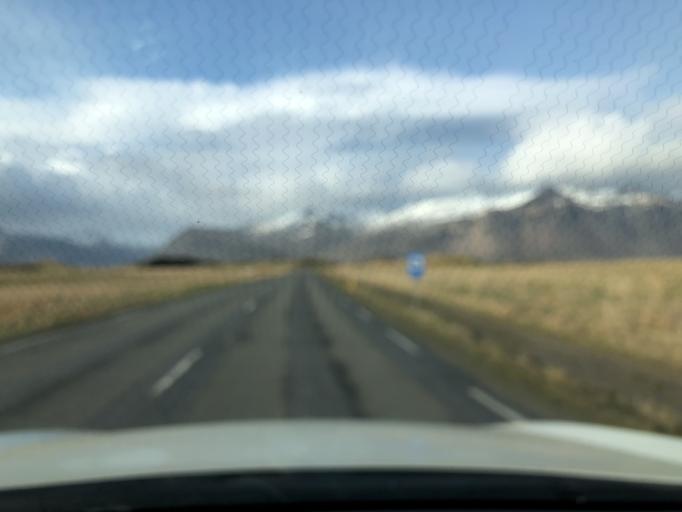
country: IS
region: East
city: Hoefn
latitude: 64.2753
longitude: -15.2014
